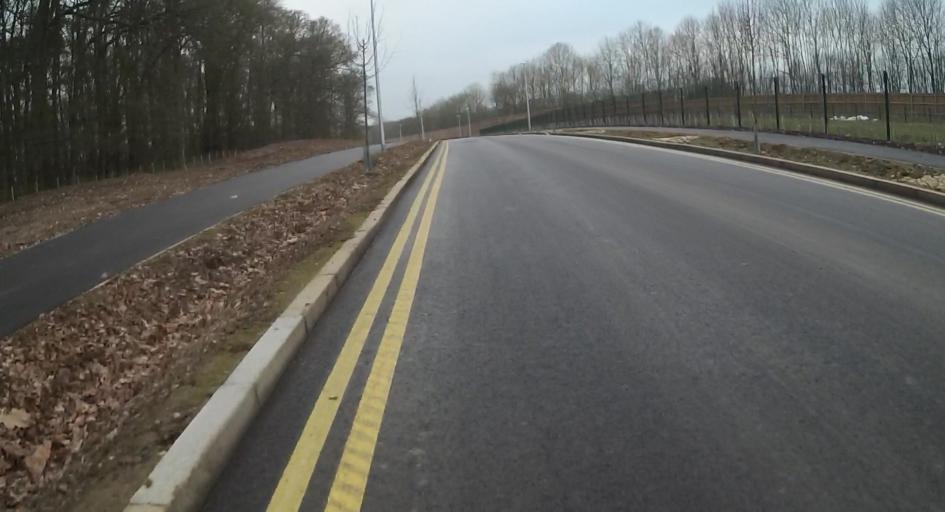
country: GB
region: England
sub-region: Wokingham
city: Wokingham
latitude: 51.4179
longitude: -0.8104
